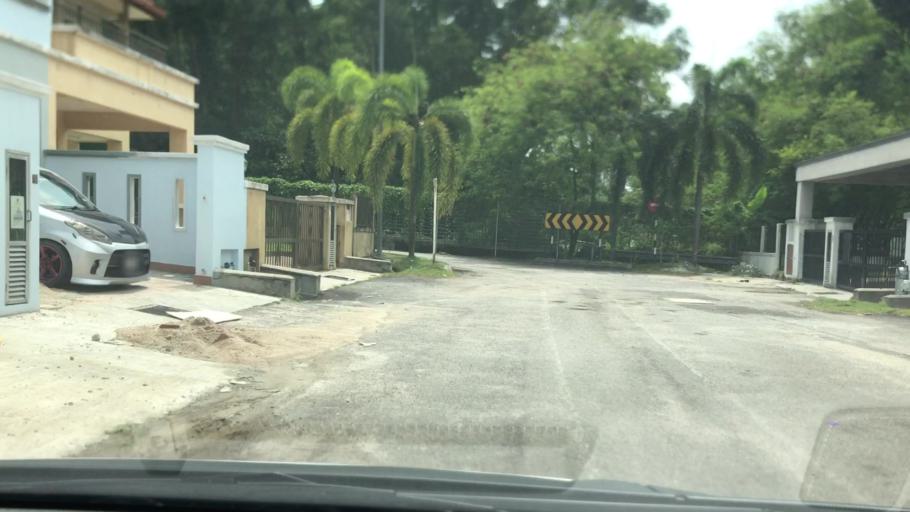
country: MY
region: Putrajaya
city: Putrajaya
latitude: 2.9885
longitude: 101.6683
